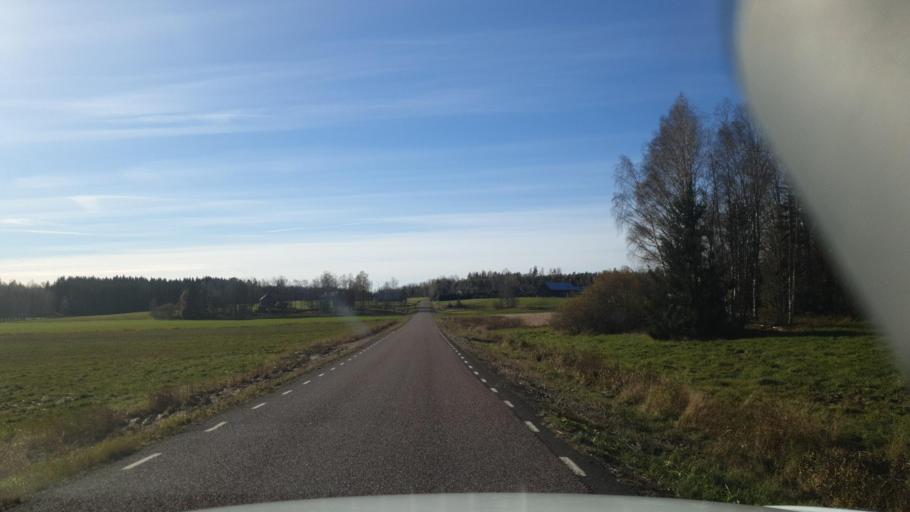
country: SE
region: Vaermland
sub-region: Karlstads Kommun
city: Edsvalla
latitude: 59.4920
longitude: 13.0992
